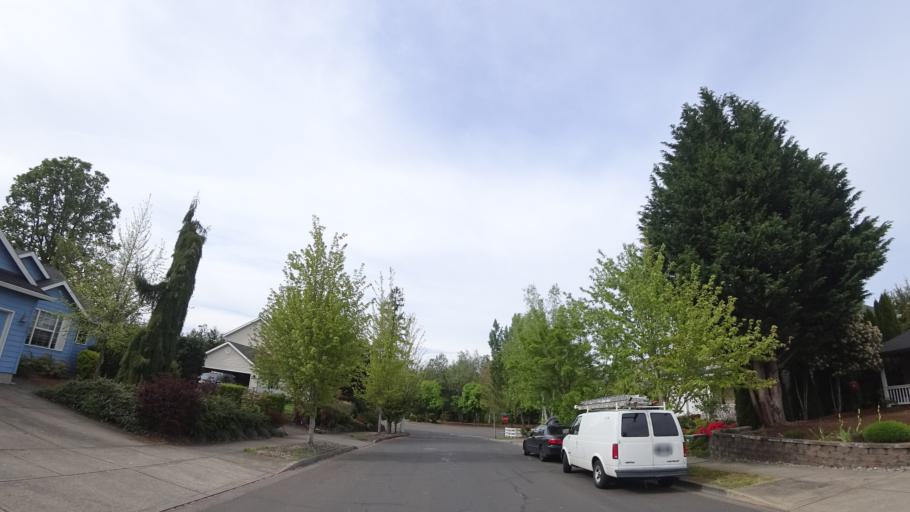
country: US
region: Oregon
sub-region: Washington County
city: Aloha
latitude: 45.5081
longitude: -122.9180
